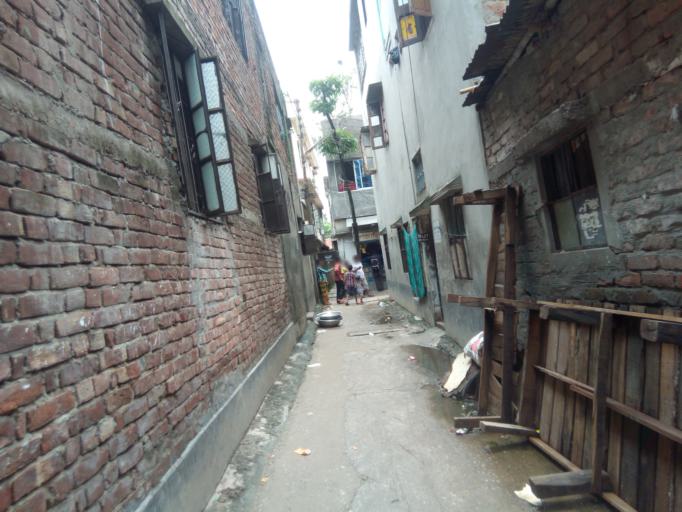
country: BD
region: Dhaka
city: Azimpur
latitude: 23.7470
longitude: 90.3668
